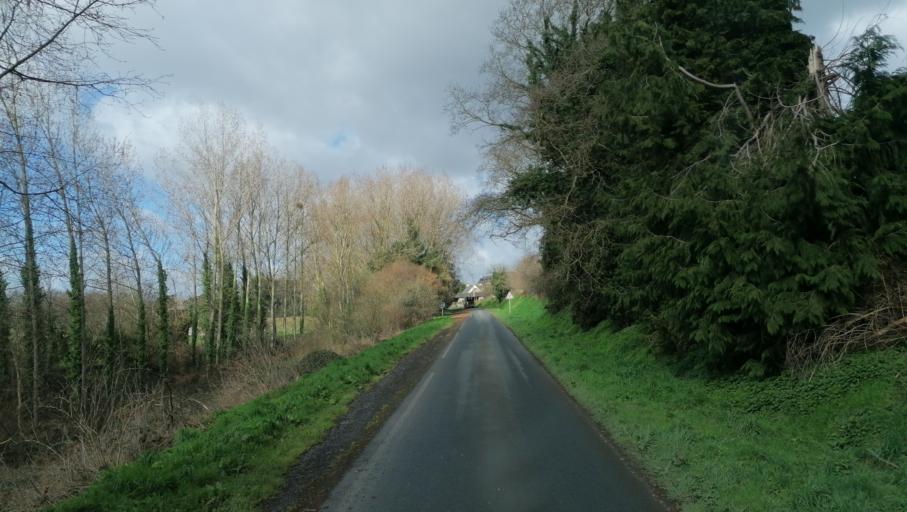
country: FR
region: Brittany
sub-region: Departement des Cotes-d'Armor
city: Plelo
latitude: 48.5755
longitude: -2.9152
